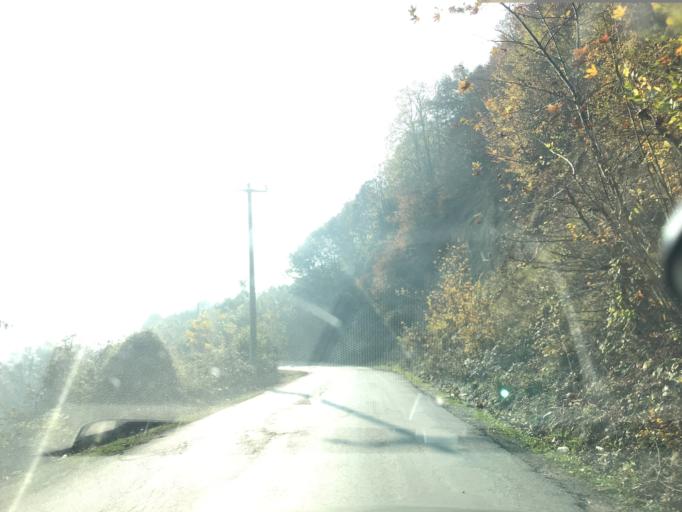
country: TR
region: Duzce
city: Cumayeri
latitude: 40.9117
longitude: 30.9444
